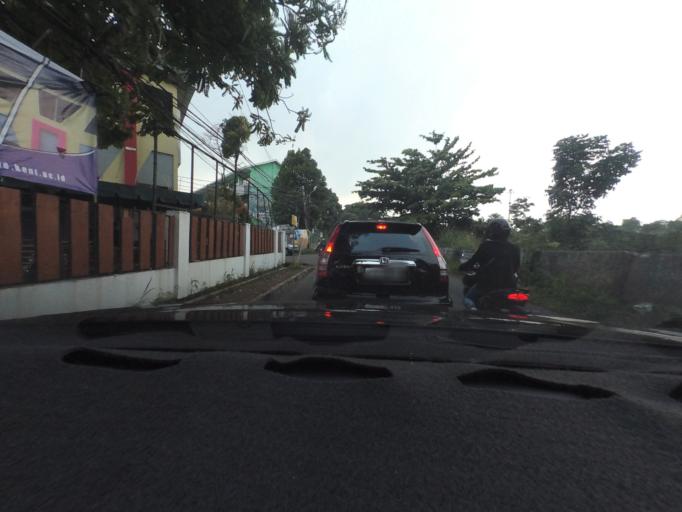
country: ID
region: West Java
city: Bogor
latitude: -6.6017
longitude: 106.8121
